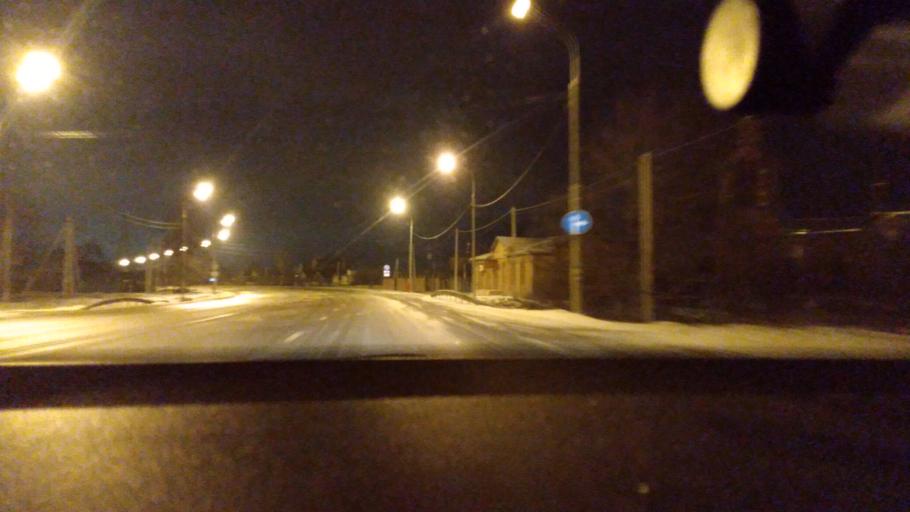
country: RU
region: Moskovskaya
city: Bronnitsy
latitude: 55.3947
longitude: 38.3225
